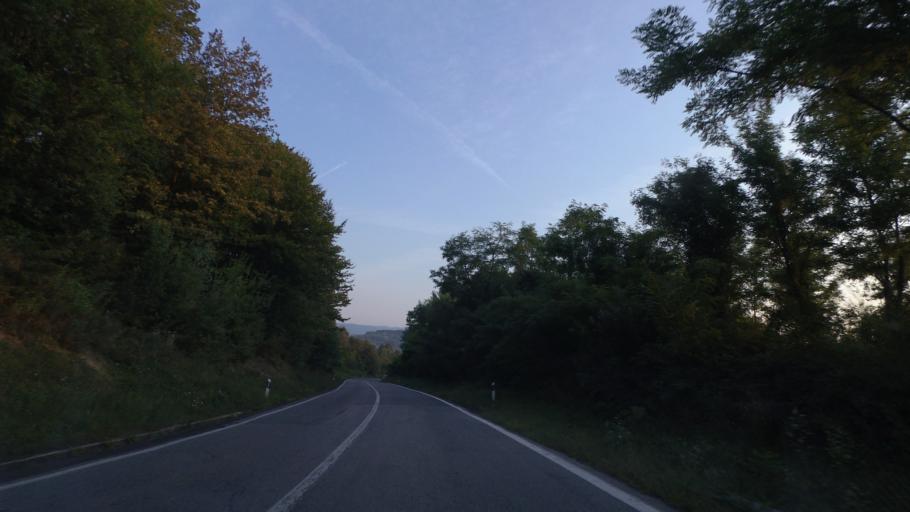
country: HR
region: Brodsko-Posavska
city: Cernik
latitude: 45.2855
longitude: 17.4177
